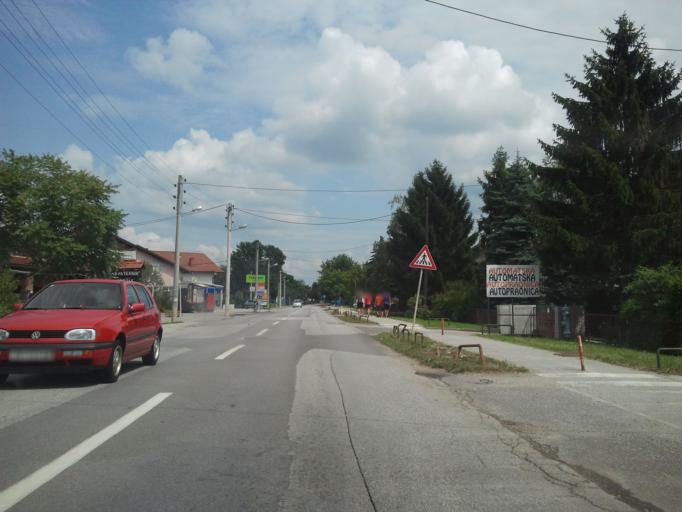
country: HR
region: Grad Zagreb
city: Lucko
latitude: 45.7608
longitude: 15.8759
